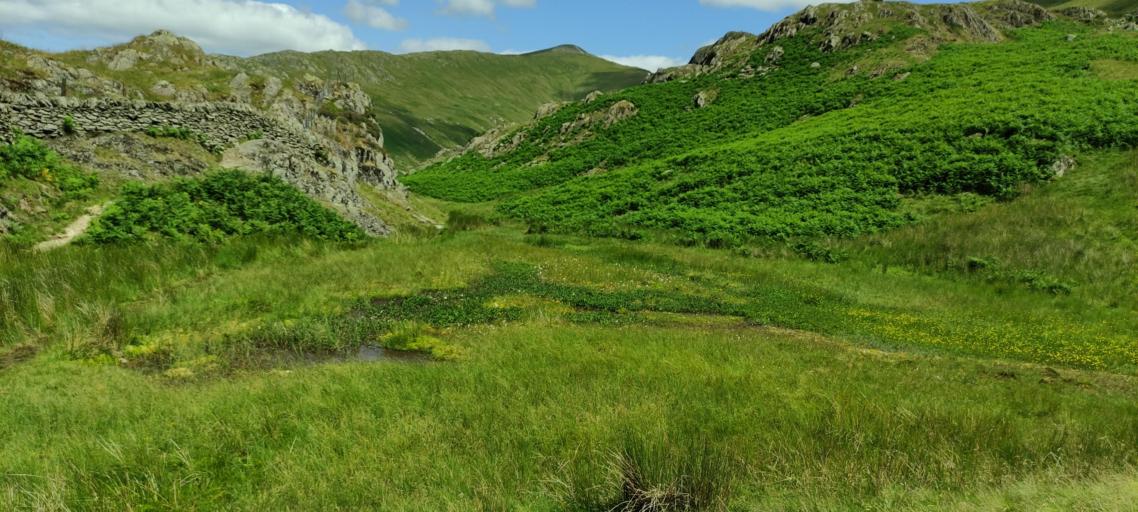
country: GB
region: England
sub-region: Cumbria
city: Ambleside
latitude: 54.4633
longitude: -3.0062
